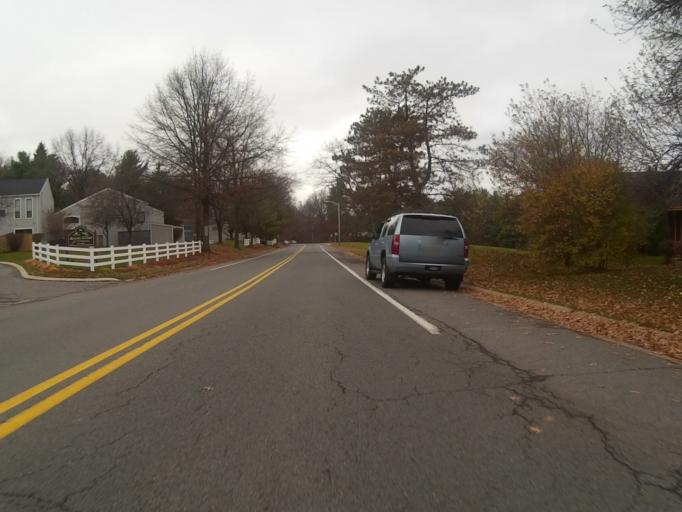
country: US
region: Pennsylvania
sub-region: Centre County
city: Park Forest Village
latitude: 40.8291
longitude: -77.8877
